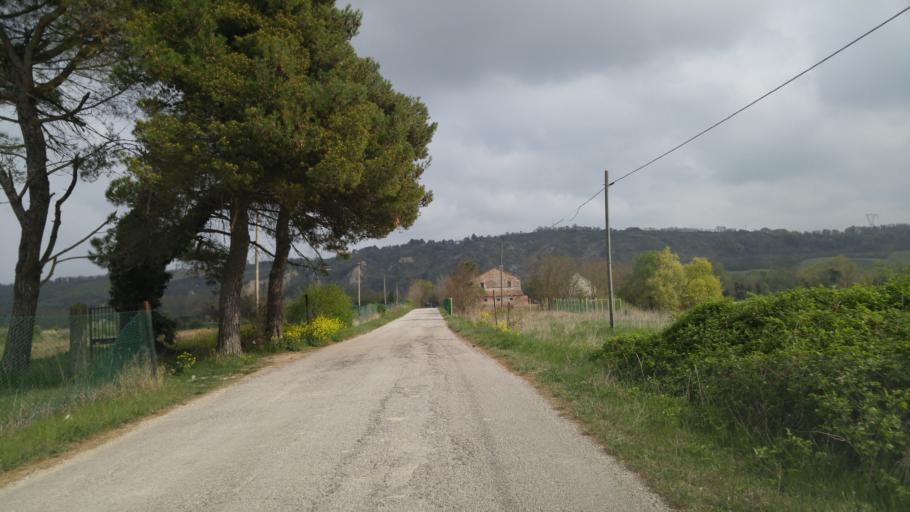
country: IT
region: The Marches
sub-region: Provincia di Pesaro e Urbino
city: Bellocchi
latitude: 43.7747
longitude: 12.9847
